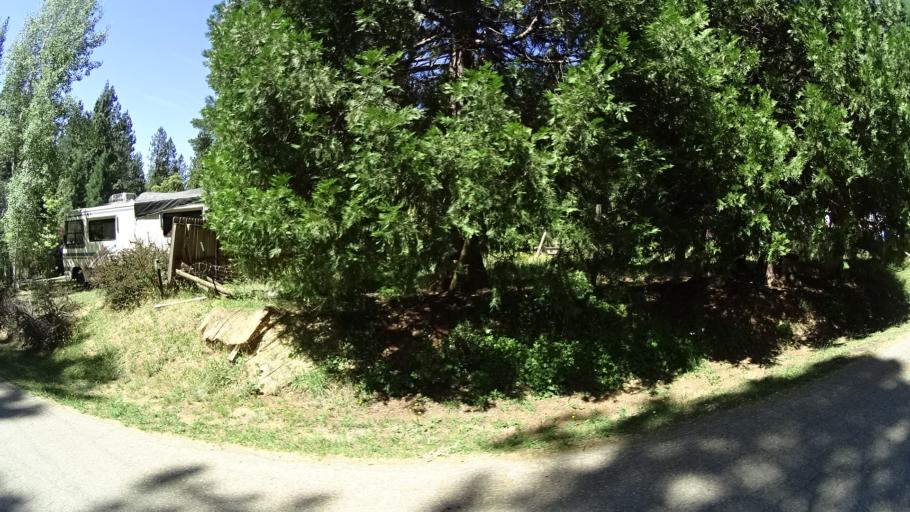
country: US
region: California
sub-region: Amador County
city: Pioneer
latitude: 38.4444
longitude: -120.4286
